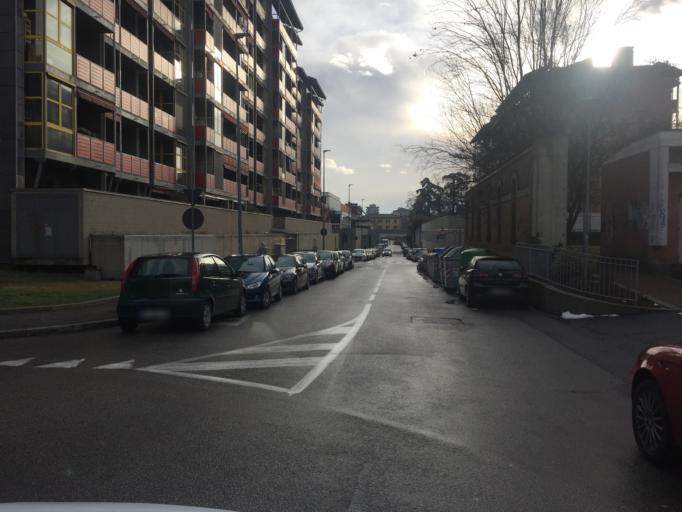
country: IT
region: Emilia-Romagna
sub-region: Provincia di Bologna
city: Bologna
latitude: 44.5058
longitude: 11.3040
